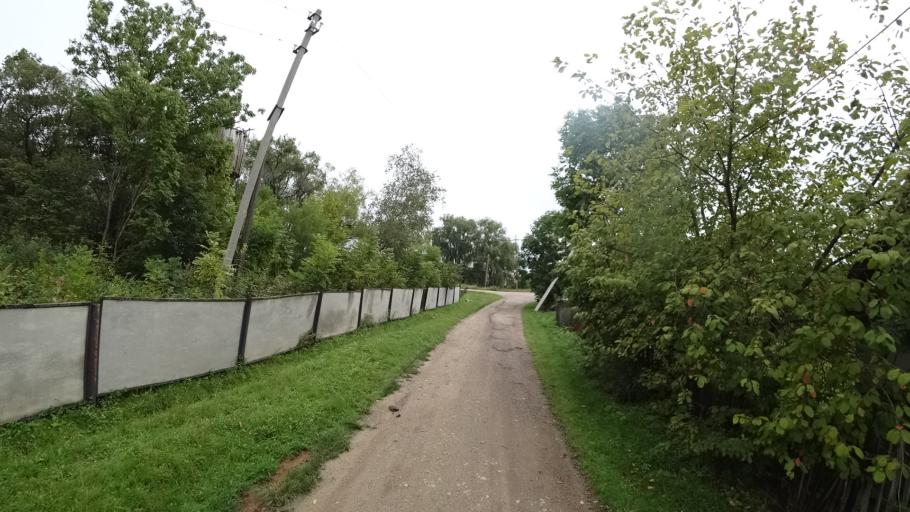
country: RU
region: Primorskiy
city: Monastyrishche
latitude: 44.0818
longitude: 132.5834
